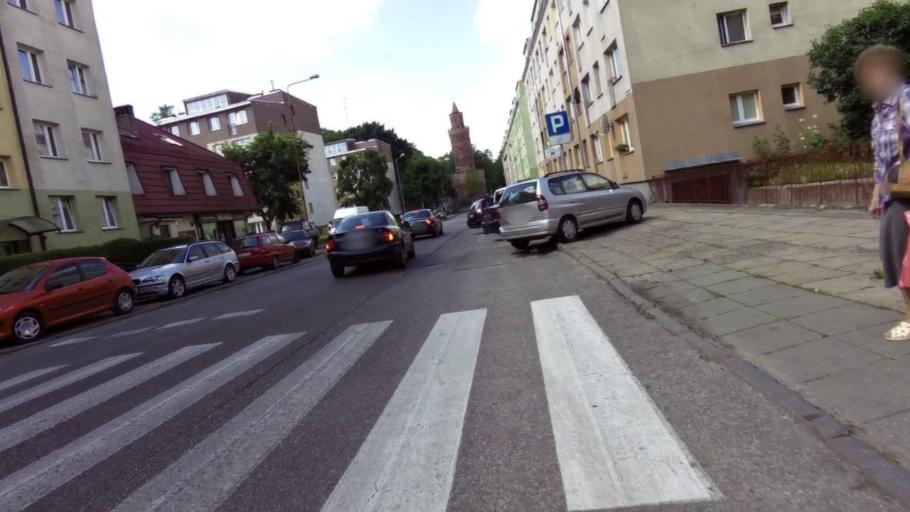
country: PL
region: West Pomeranian Voivodeship
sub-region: Powiat stargardzki
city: Stargard Szczecinski
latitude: 53.3356
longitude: 15.0456
